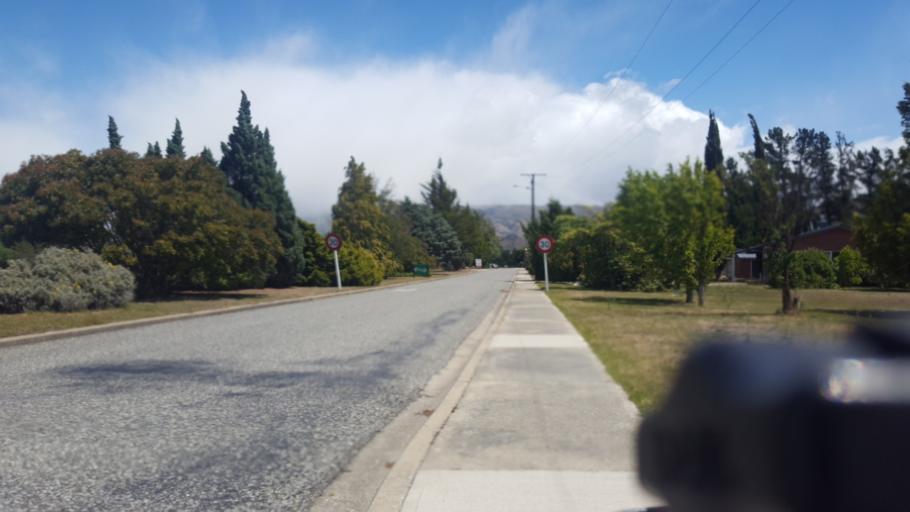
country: NZ
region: Otago
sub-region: Queenstown-Lakes District
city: Wanaka
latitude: -45.1990
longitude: 169.3321
